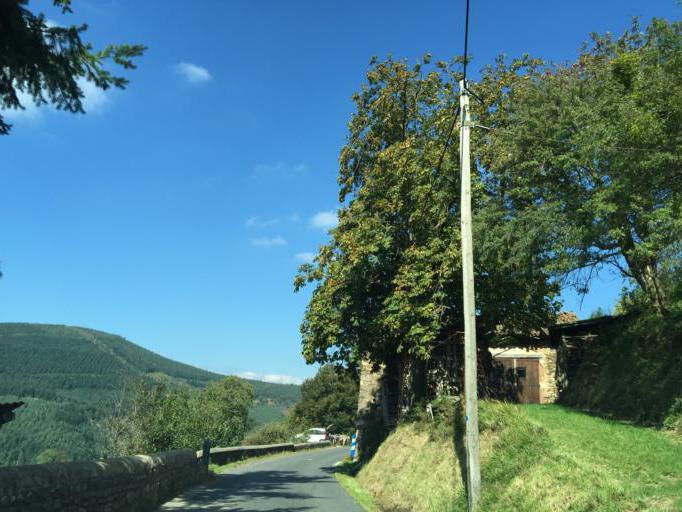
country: FR
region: Rhone-Alpes
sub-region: Departement de la Loire
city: Saint-Paul-en-Jarez
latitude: 45.4205
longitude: 4.5641
